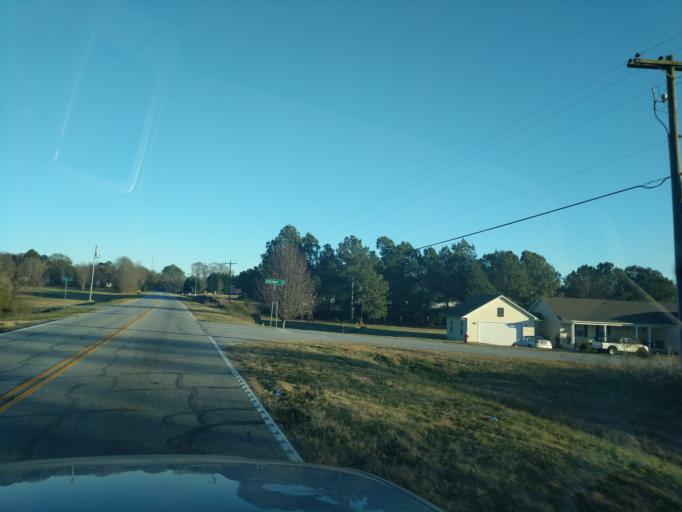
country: US
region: South Carolina
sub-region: Oconee County
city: Utica
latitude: 34.5635
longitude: -82.8835
